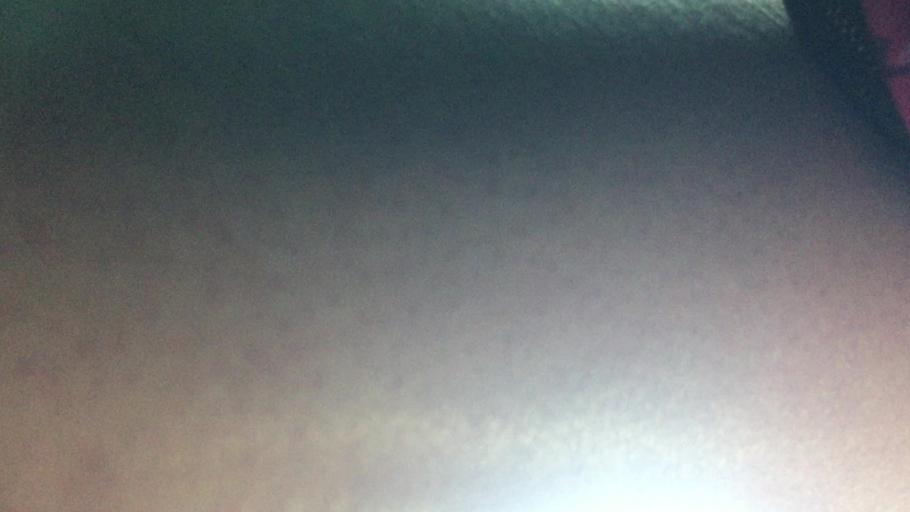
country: US
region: Georgia
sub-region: Carroll County
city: Carrollton
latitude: 33.5962
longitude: -85.0366
